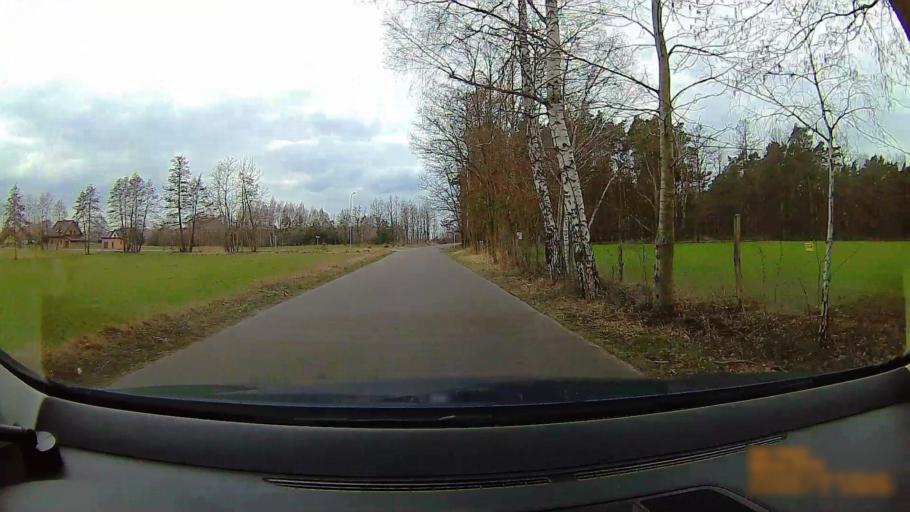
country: PL
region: Greater Poland Voivodeship
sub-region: Powiat koninski
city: Rychwal
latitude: 52.0804
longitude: 18.1346
